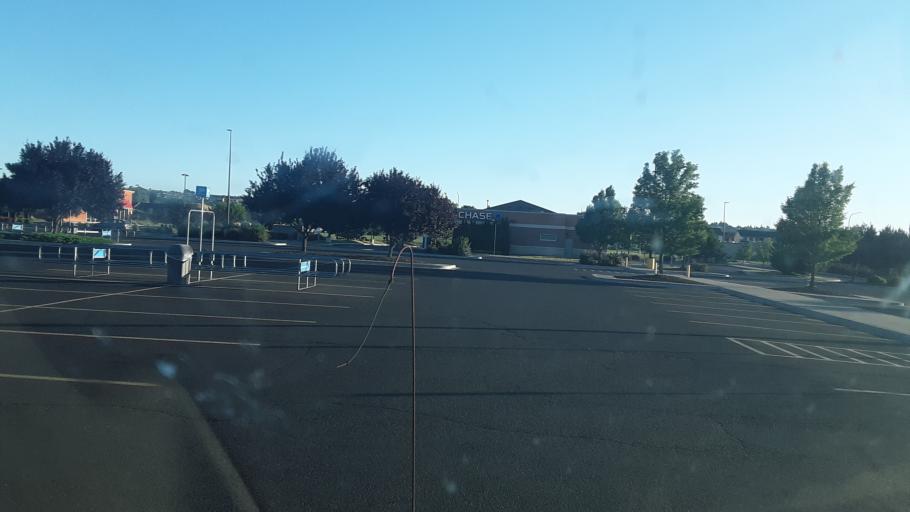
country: US
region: Washington
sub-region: Yakima County
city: West Valley
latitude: 46.5842
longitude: -120.5968
